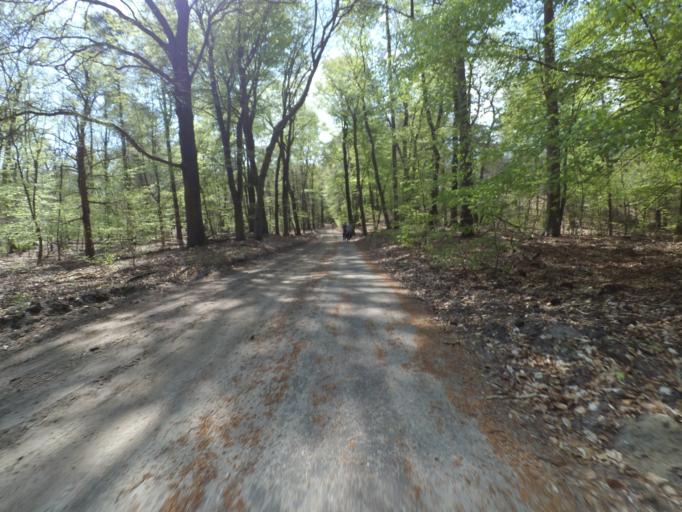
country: NL
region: Gelderland
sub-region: Gemeente Harderwijk
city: Harderwijk
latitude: 52.3242
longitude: 5.7027
